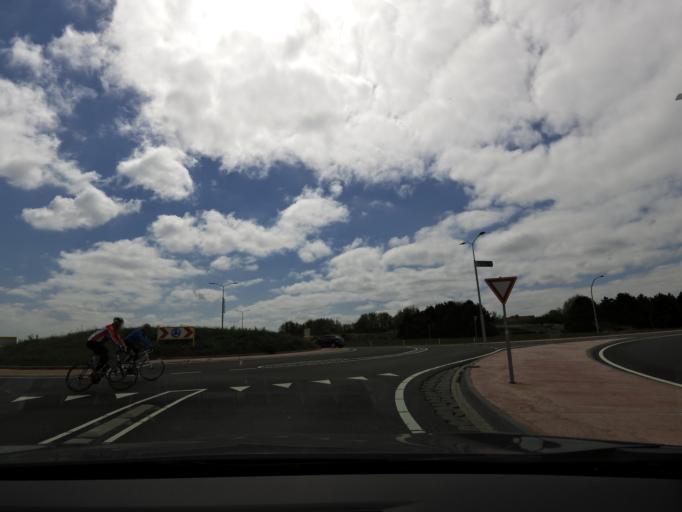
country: NL
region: South Holland
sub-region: Gemeente Goeree-Overflakkee
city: Ouddorp
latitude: 51.8087
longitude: 3.9448
